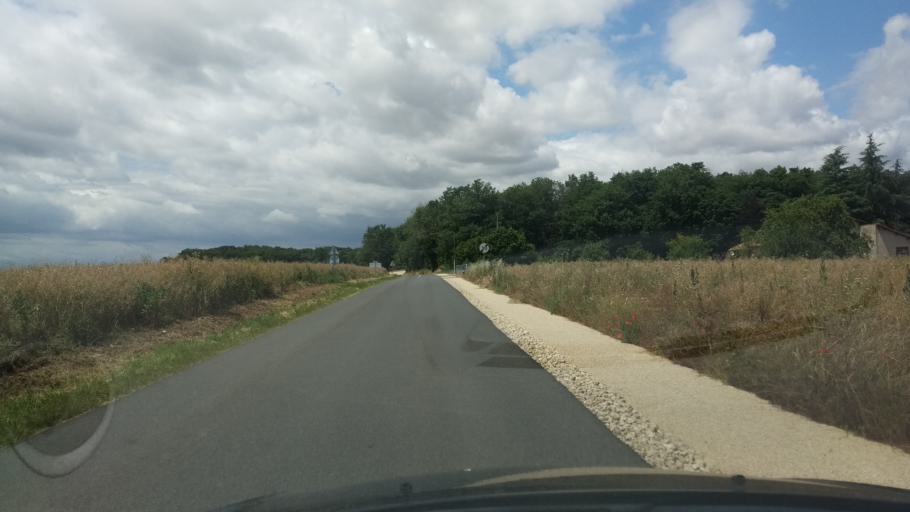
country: FR
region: Poitou-Charentes
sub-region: Departement de la Vienne
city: Cisse
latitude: 46.6114
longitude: 0.2274
